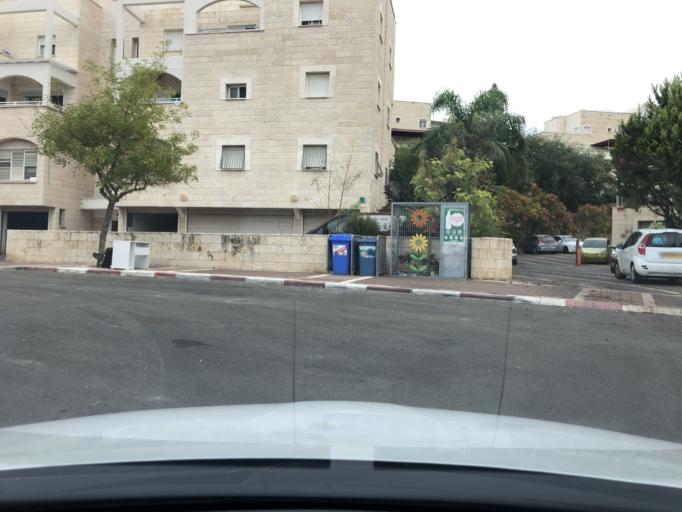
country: IL
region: Central District
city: Modiin
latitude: 31.9029
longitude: 35.0099
